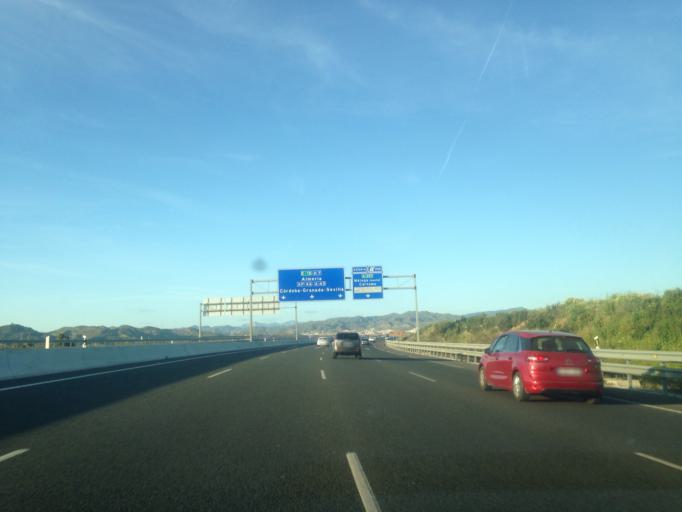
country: ES
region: Andalusia
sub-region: Provincia de Malaga
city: Alhaurin de la Torre
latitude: 36.6914
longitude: -4.5256
